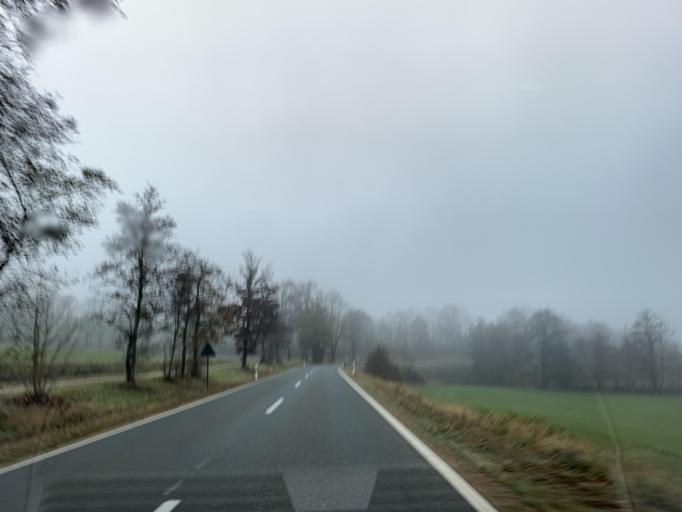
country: DE
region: Bavaria
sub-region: Upper Palatinate
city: Neunburg vorm Wald
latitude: 49.3586
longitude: 12.3972
